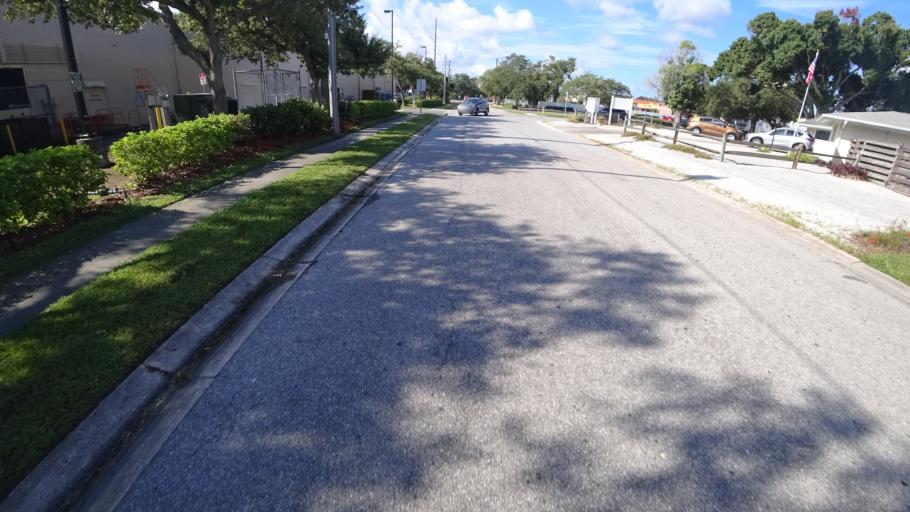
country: US
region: Florida
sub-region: Manatee County
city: South Bradenton
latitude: 27.4638
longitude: -82.5855
